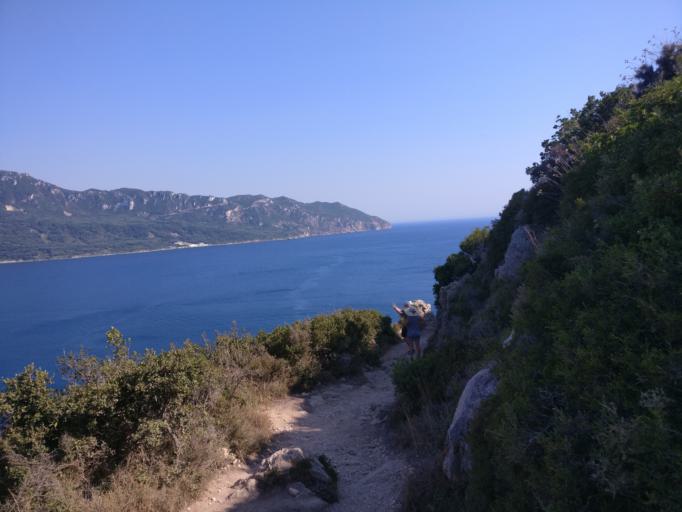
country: GR
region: Ionian Islands
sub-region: Nomos Kerkyras
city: Agios Georgis
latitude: 39.7168
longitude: 19.6588
